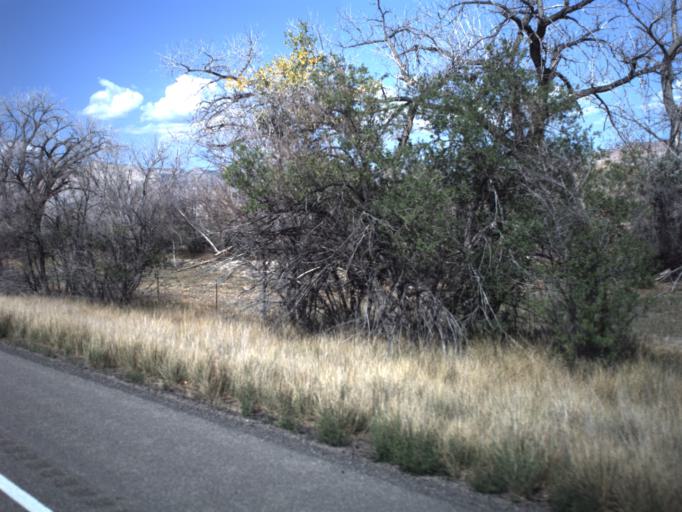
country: US
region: Utah
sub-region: Emery County
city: Orangeville
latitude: 39.1680
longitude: -111.0599
